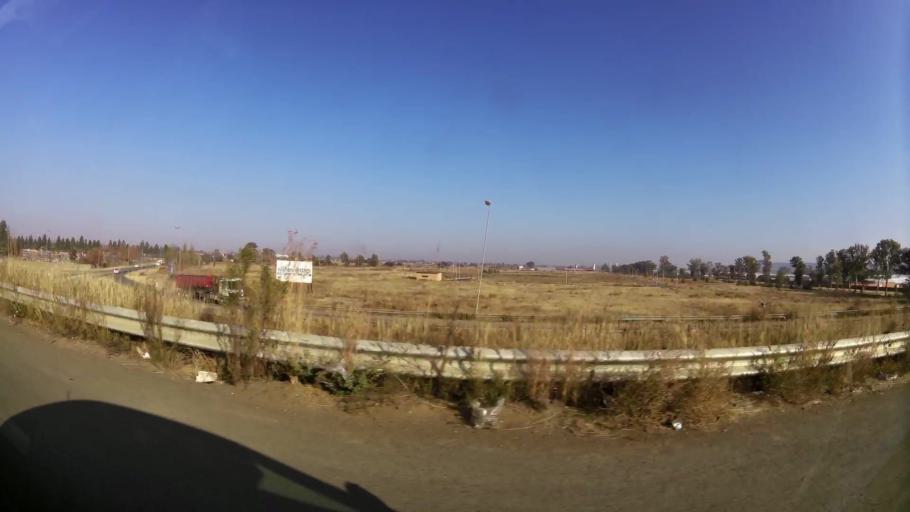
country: ZA
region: Orange Free State
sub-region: Mangaung Metropolitan Municipality
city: Bloemfontein
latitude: -29.1357
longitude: 26.2671
